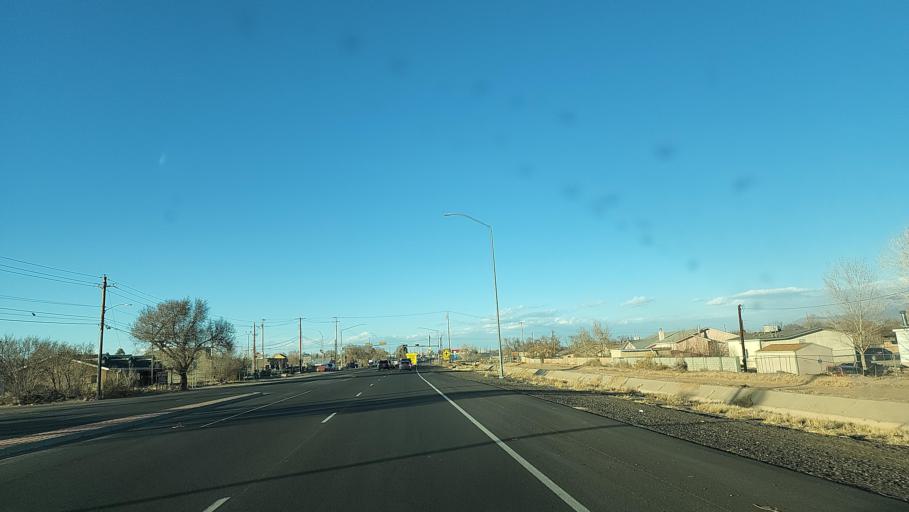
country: US
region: New Mexico
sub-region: Bernalillo County
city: South Valley
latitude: 35.0288
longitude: -106.7137
